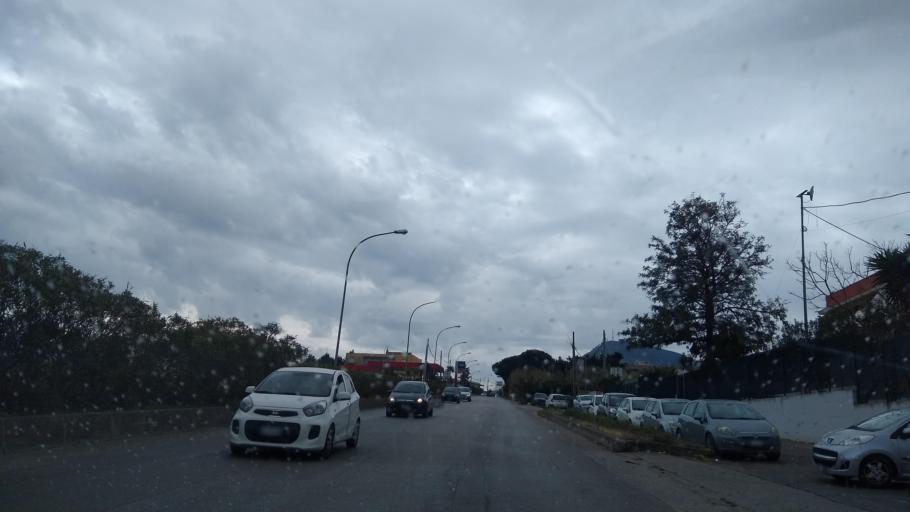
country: IT
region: Sicily
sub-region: Trapani
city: Alcamo
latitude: 37.9981
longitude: 12.9579
